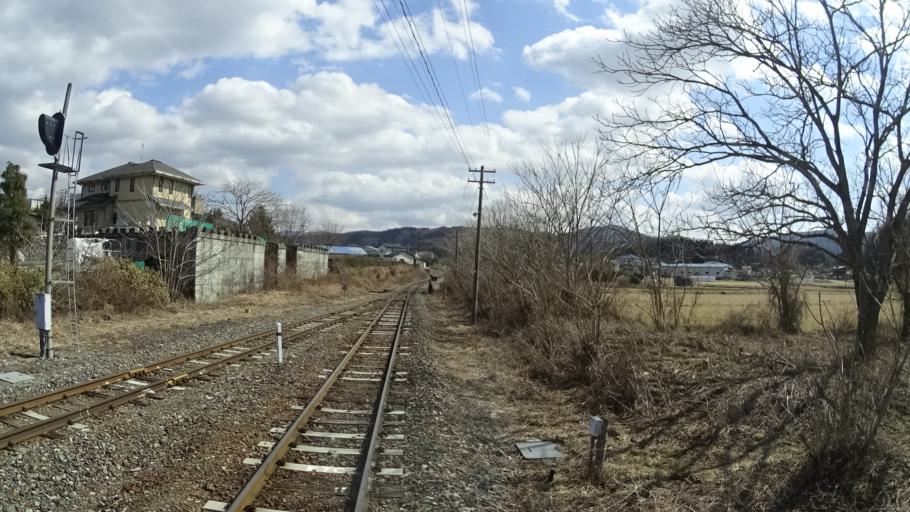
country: JP
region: Iwate
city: Tono
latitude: 39.2838
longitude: 141.5866
